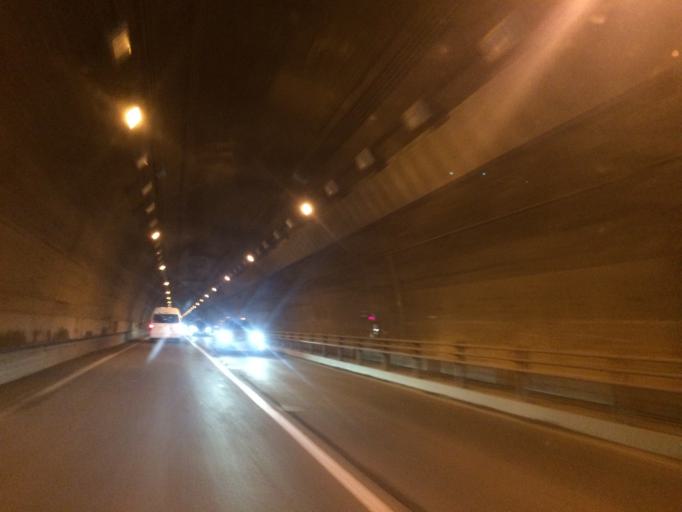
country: JP
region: Hokkaido
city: Otaru
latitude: 43.2103
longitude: 140.9100
